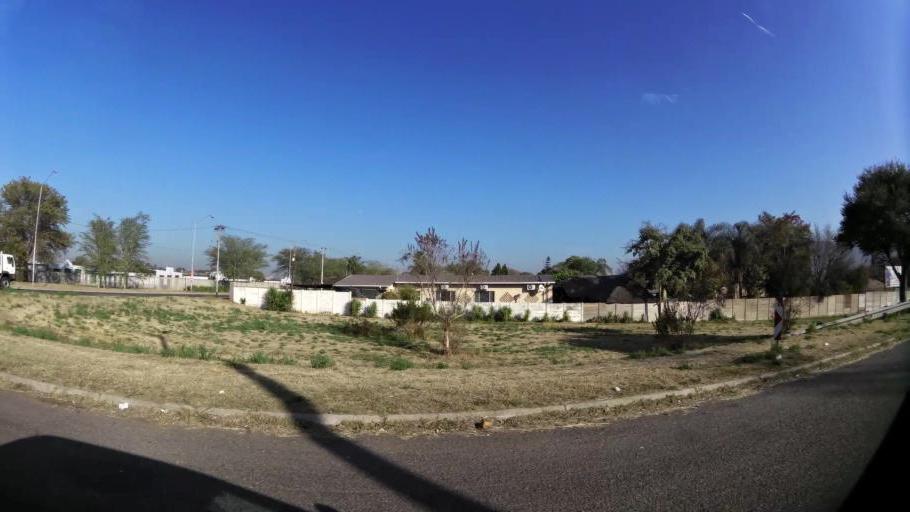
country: ZA
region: Gauteng
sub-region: City of Tshwane Metropolitan Municipality
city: Pretoria
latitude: -25.7059
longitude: 28.1719
